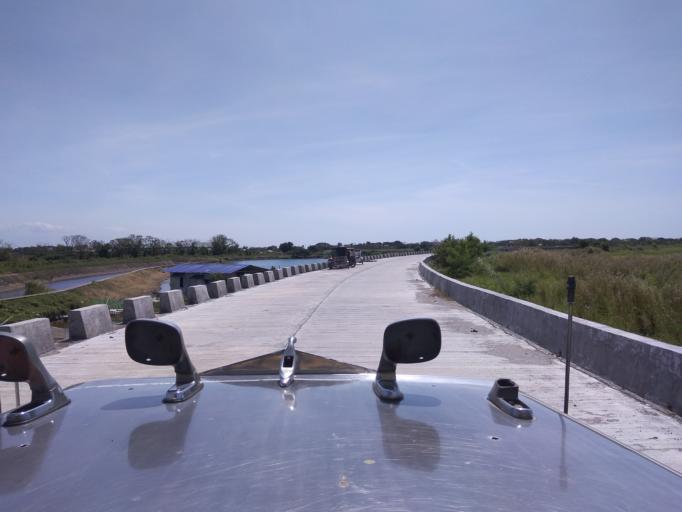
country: PH
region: Central Luzon
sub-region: Province of Pampanga
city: Minalin
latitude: 14.9880
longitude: 120.6944
